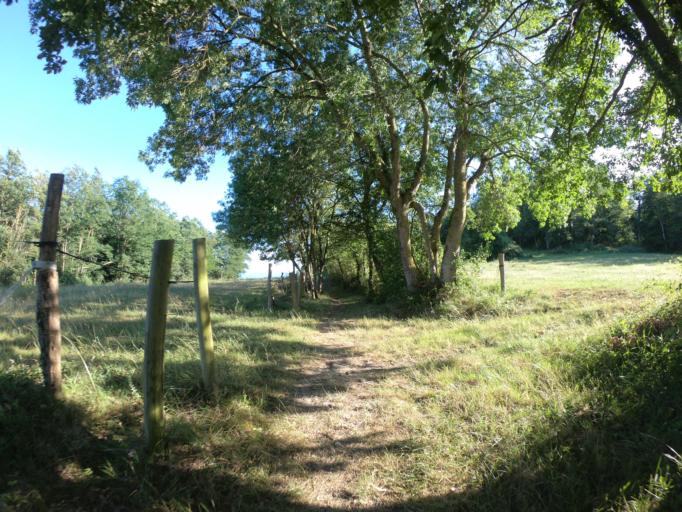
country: FR
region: Midi-Pyrenees
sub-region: Departement de l'Ariege
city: La Tour-du-Crieu
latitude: 43.1053
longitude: 1.7174
